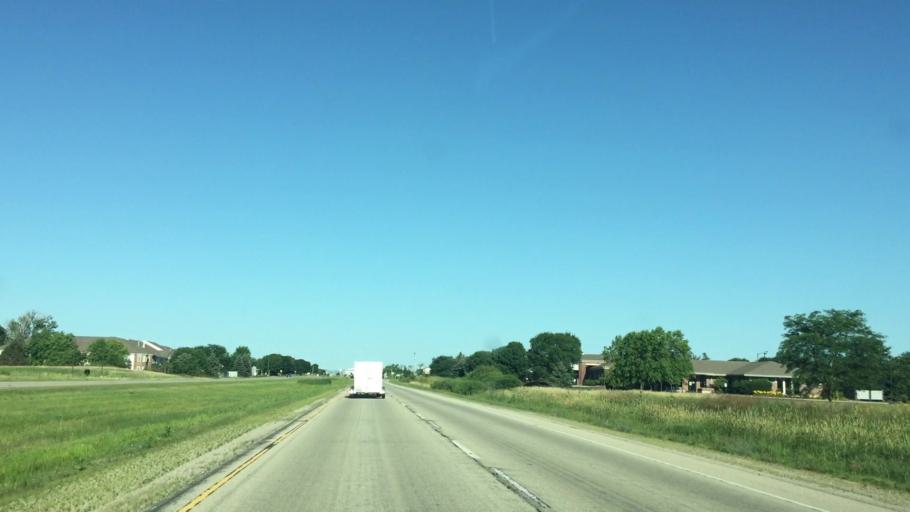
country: US
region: Wisconsin
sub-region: Winnebago County
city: Menasha
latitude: 44.2623
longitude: -88.4915
